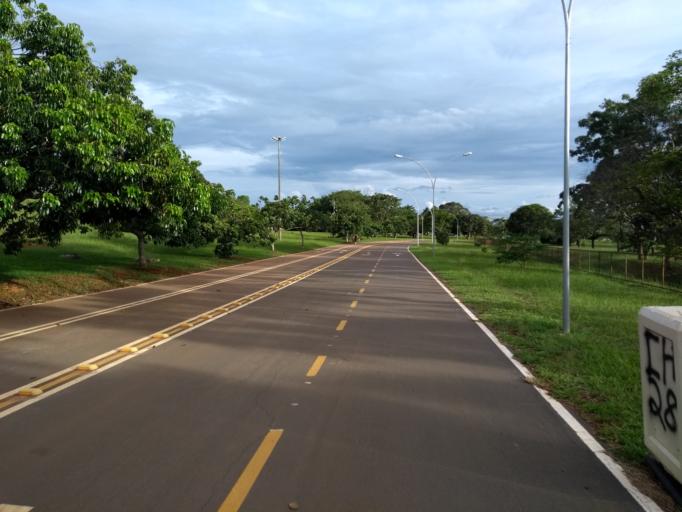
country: BR
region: Federal District
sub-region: Brasilia
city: Brasilia
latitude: -15.8059
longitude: -47.9159
